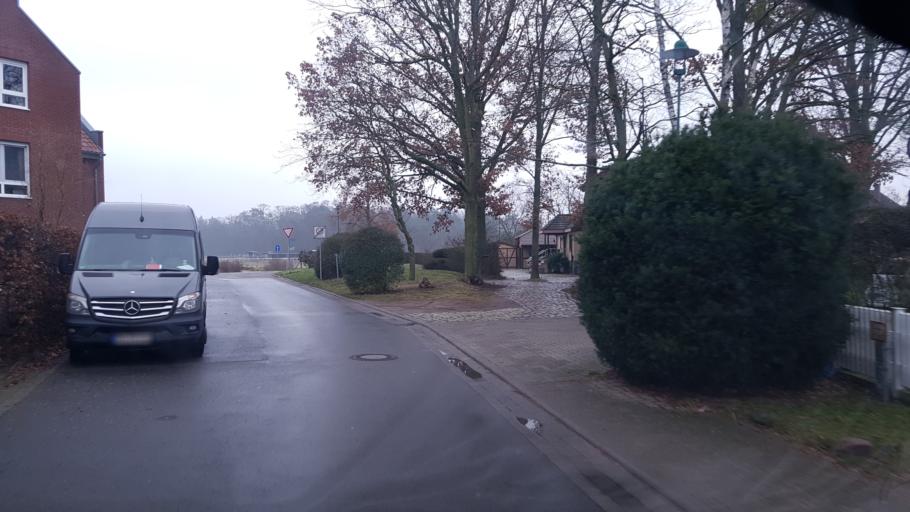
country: DE
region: Brandenburg
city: Stahnsdorf
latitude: 52.3733
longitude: 13.2190
